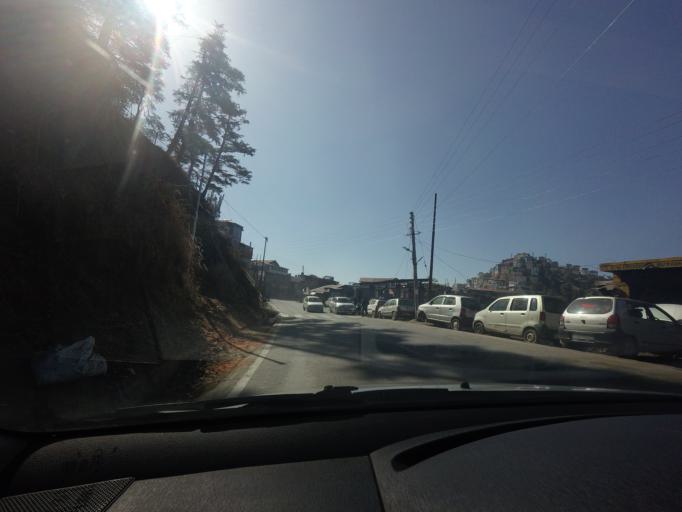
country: IN
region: Himachal Pradesh
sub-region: Shimla
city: Shimla
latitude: 31.1091
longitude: 77.2140
